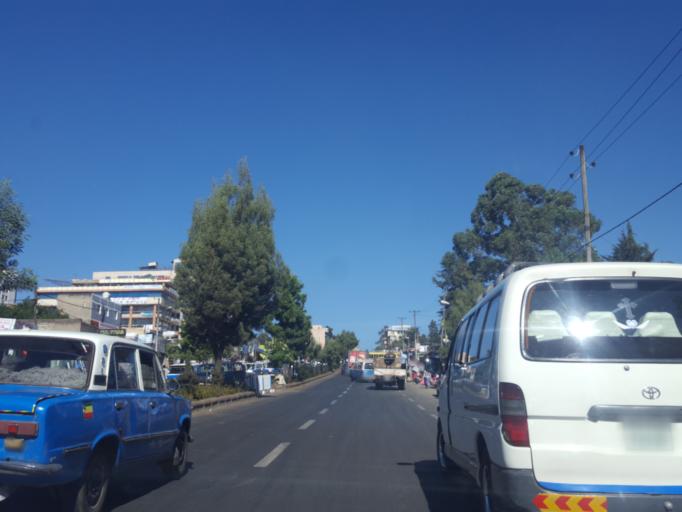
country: ET
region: Adis Abeba
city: Addis Ababa
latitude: 9.0584
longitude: 38.7387
